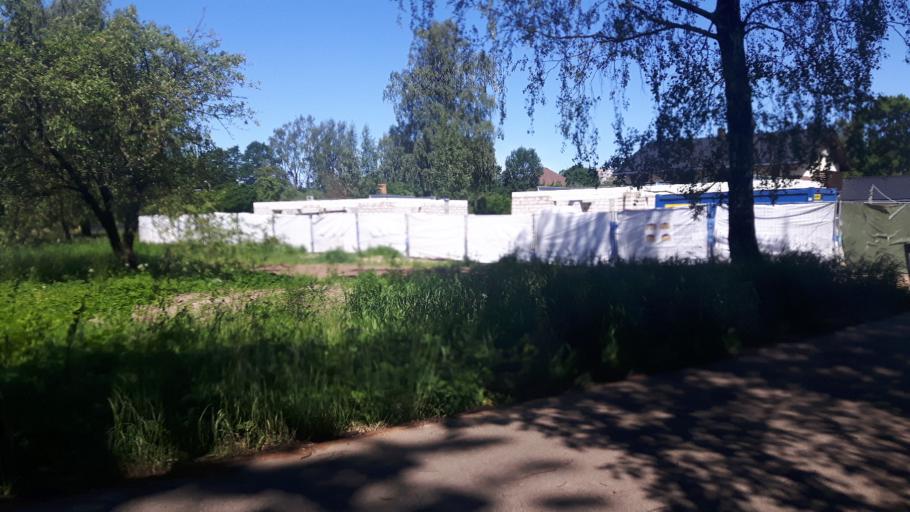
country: LV
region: Marupe
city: Marupe
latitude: 56.9483
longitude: 24.0312
